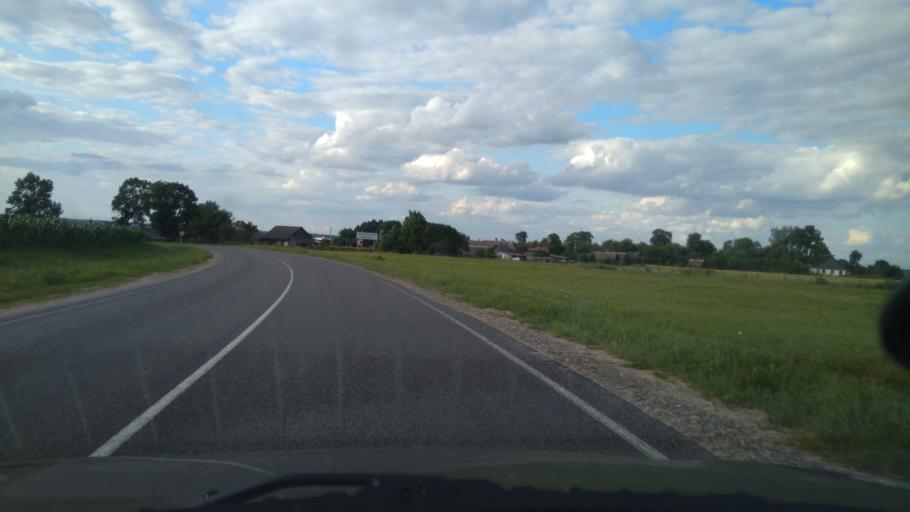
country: BY
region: Grodnenskaya
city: Masty
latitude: 53.3104
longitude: 24.6962
